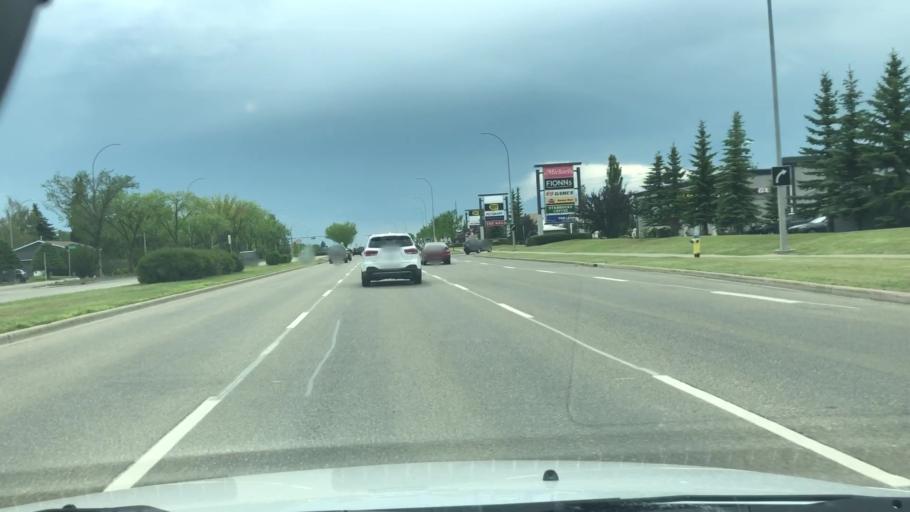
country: CA
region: Alberta
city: St. Albert
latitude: 53.5995
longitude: -113.5581
